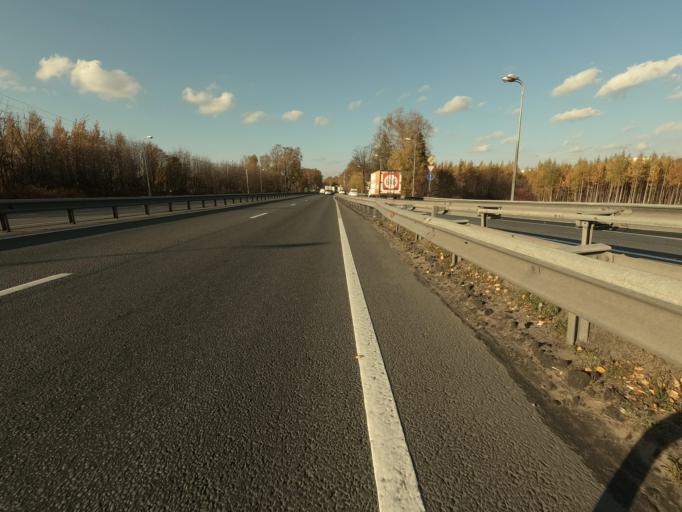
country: RU
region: St.-Petersburg
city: Pargolovo
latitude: 60.1014
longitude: 30.2506
